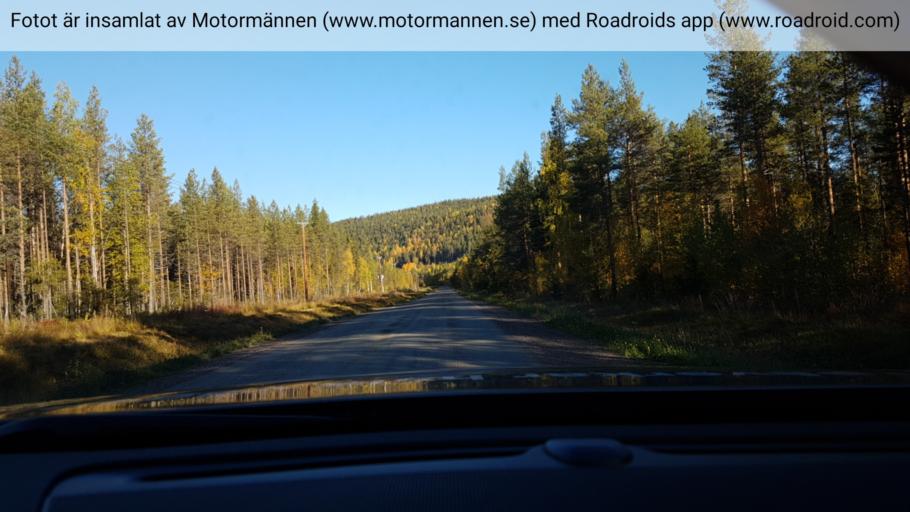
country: SE
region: Norrbotten
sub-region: Alvsbyns Kommun
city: AElvsbyn
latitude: 66.1689
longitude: 21.2439
